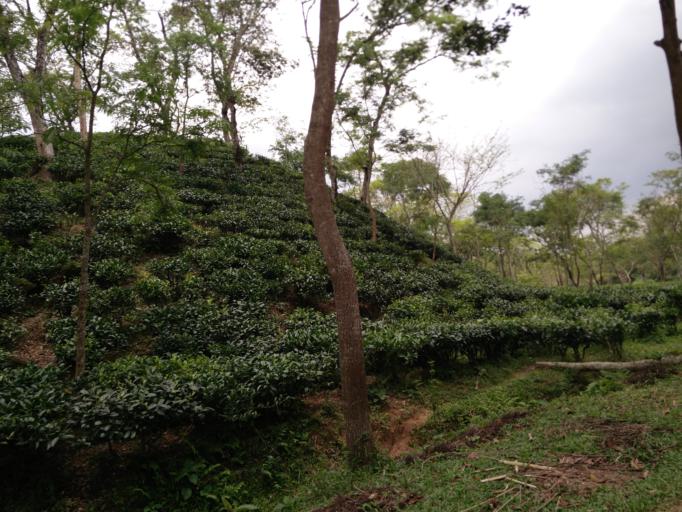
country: IN
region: Tripura
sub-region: Dhalai
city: Kamalpur
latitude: 24.3061
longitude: 91.8011
